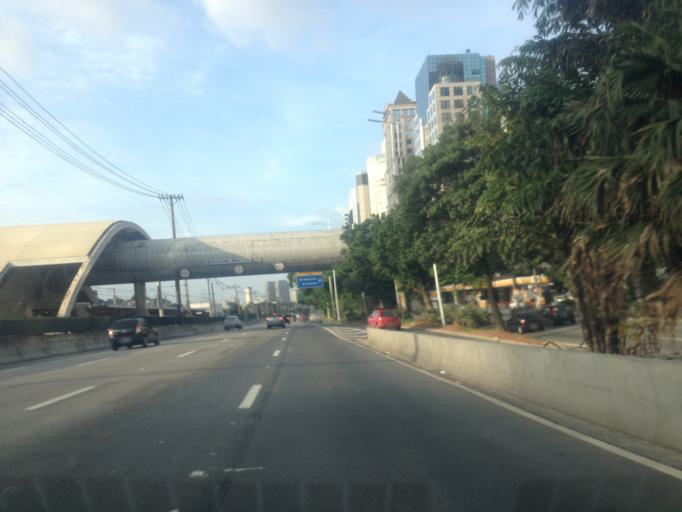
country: BR
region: Sao Paulo
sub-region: Sao Paulo
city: Sao Paulo
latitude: -23.6054
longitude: -46.6967
